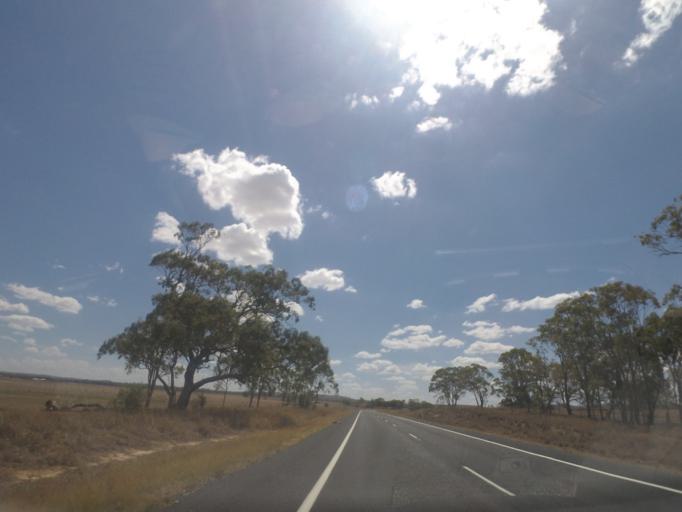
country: AU
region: Queensland
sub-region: Southern Downs
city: Warwick
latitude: -28.1784
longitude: 151.7786
